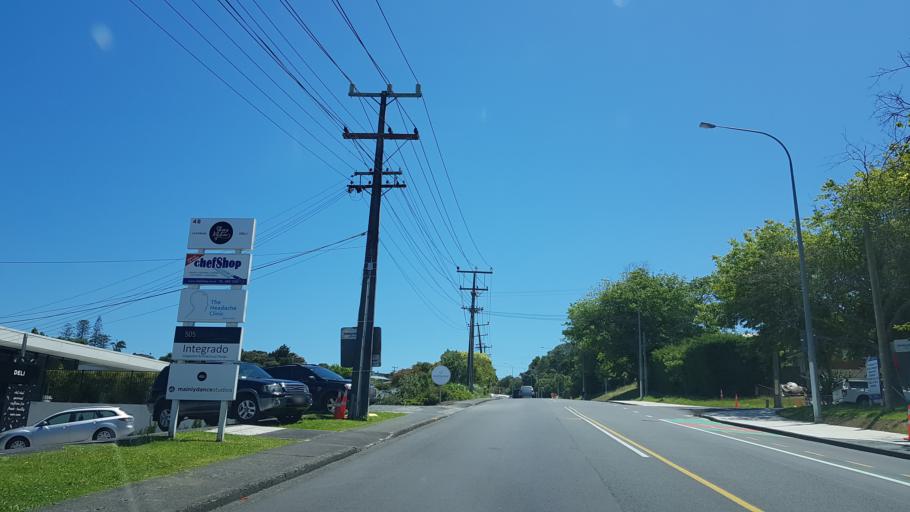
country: NZ
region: Auckland
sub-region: Auckland
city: North Shore
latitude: -36.8062
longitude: 174.7441
